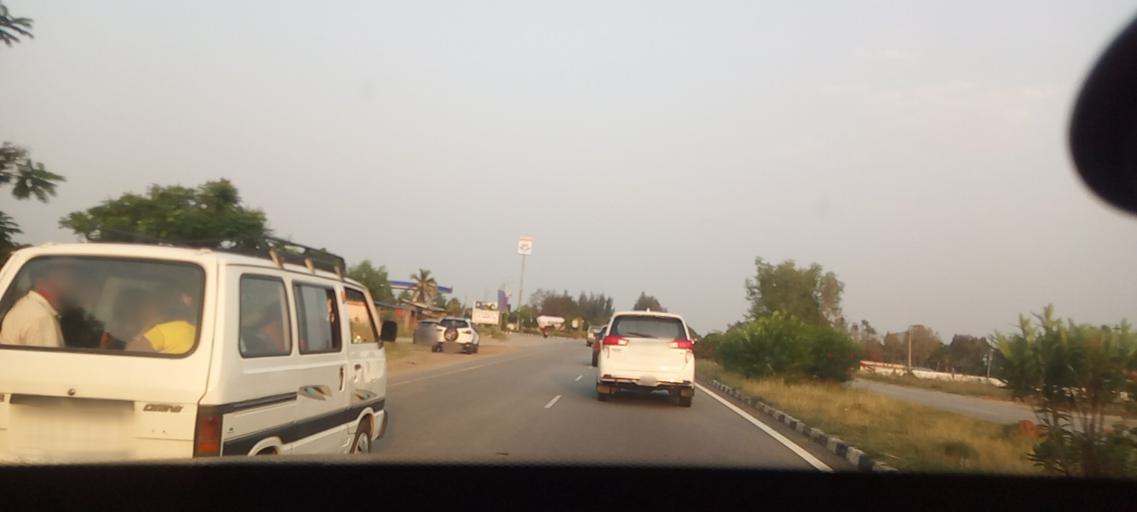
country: IN
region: Karnataka
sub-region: Tumkur
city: Kunigal
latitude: 12.9970
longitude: 76.9254
